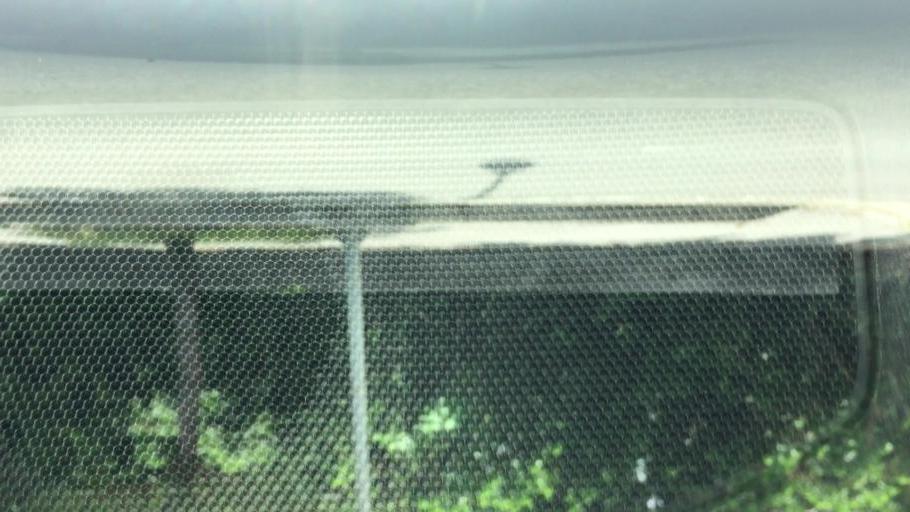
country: JP
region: Okinawa
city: Ishigaki
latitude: 24.3561
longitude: 124.1461
